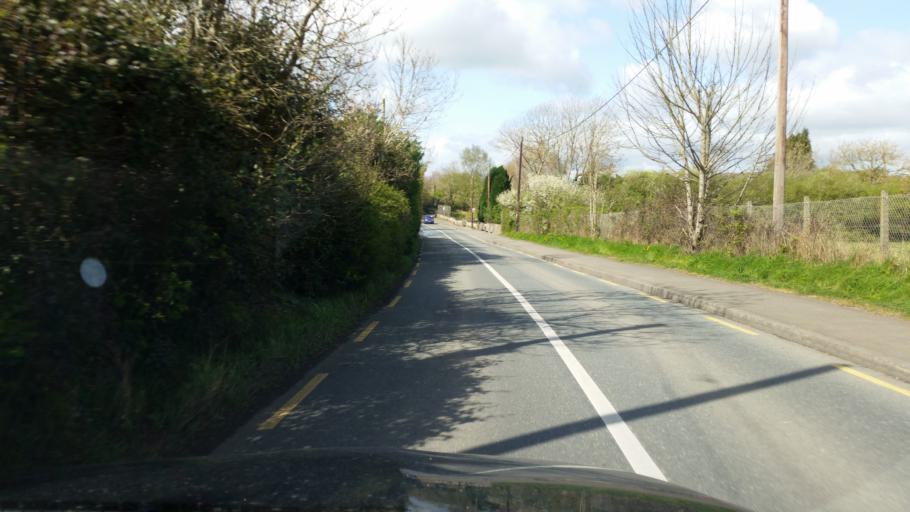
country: IE
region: Leinster
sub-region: Fingal County
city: Swords
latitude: 53.4883
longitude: -6.3072
